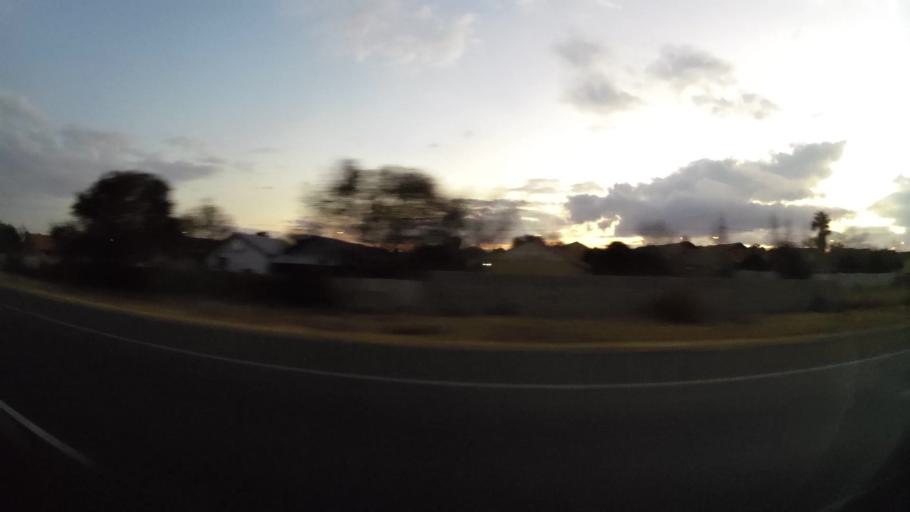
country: ZA
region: Orange Free State
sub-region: Mangaung Metropolitan Municipality
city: Bloemfontein
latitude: -29.1535
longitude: 26.1747
